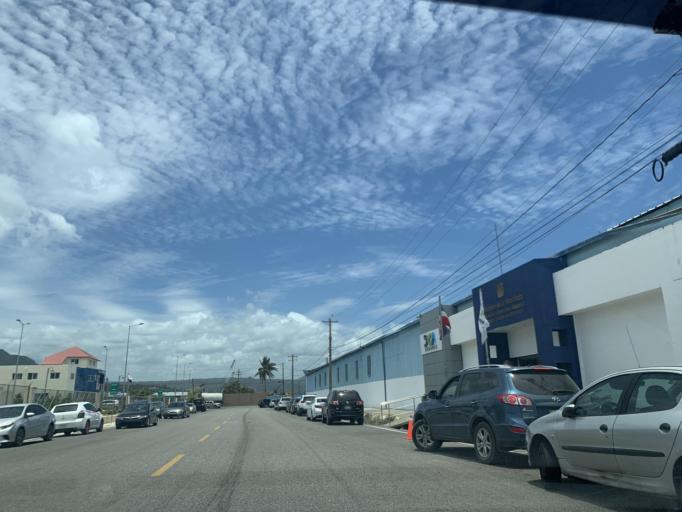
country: DO
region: Puerto Plata
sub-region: Puerto Plata
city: Puerto Plata
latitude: 19.8009
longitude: -70.6963
